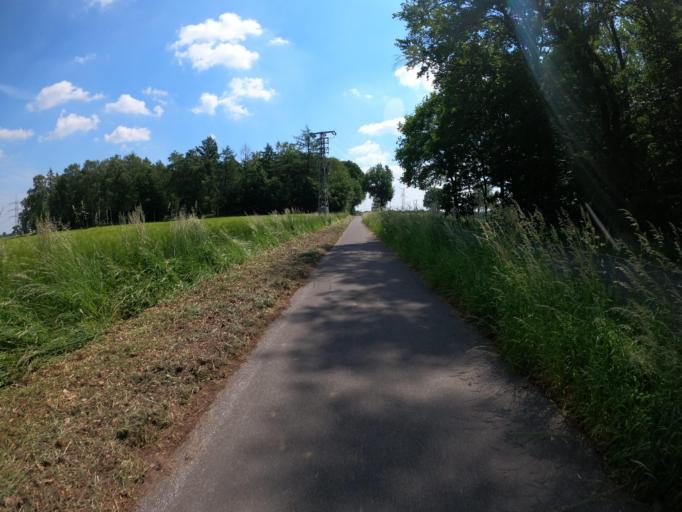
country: DE
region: North Rhine-Westphalia
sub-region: Regierungsbezirk Dusseldorf
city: Hunxe
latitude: 51.7165
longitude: 6.7364
